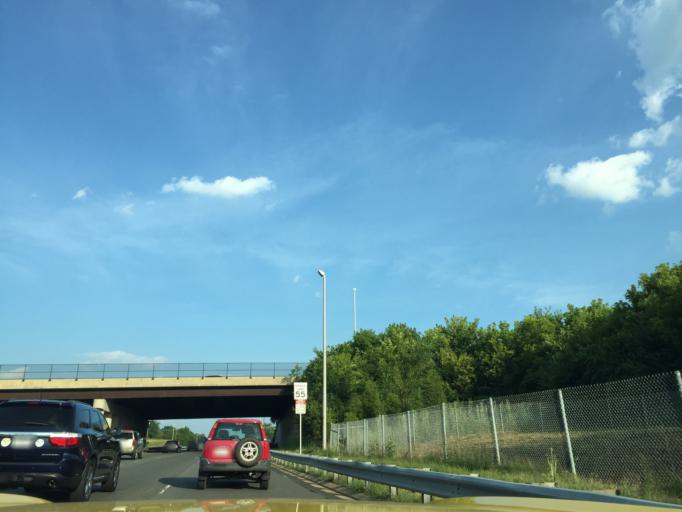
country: US
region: Virginia
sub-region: Fairfax County
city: Dranesville
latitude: 39.0110
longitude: -77.3651
